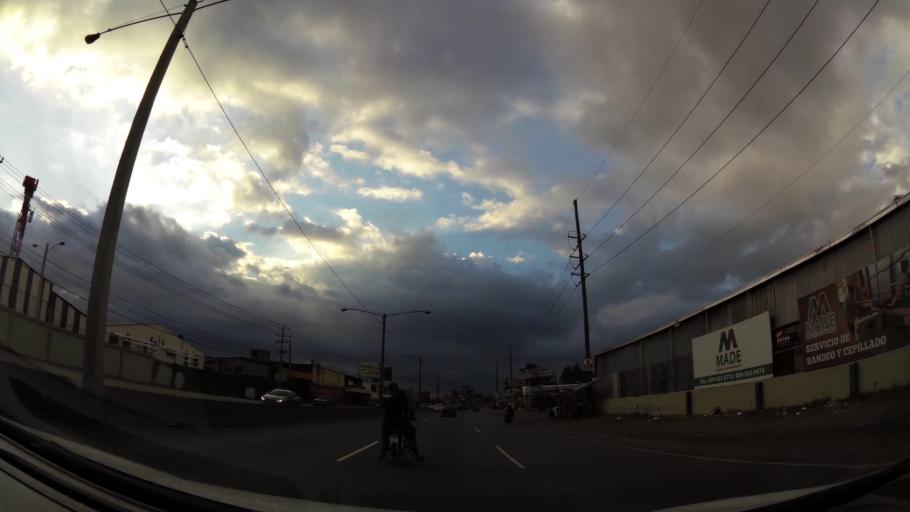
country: DO
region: Santo Domingo
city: Santo Domingo Oeste
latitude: 18.5077
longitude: -70.0053
